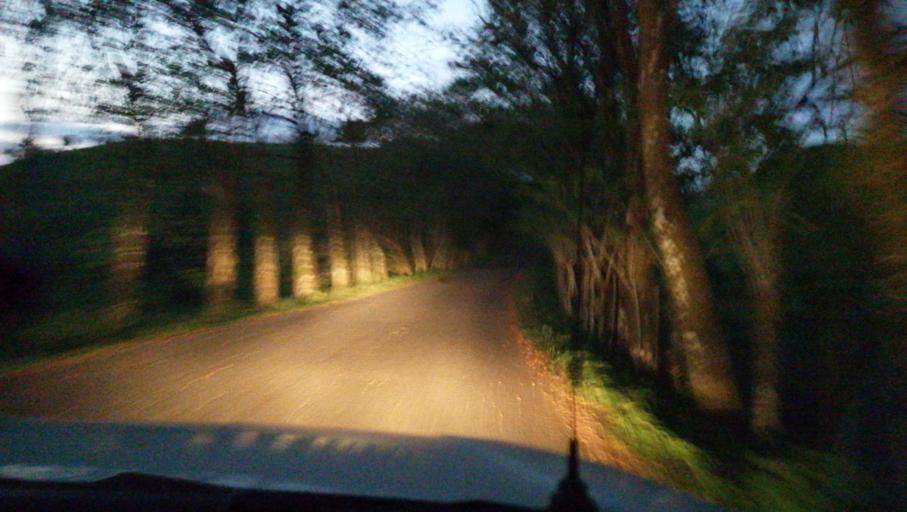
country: MX
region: Chiapas
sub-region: Ostuacan
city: Nuevo Juan del Grijalva
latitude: 17.4827
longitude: -93.3523
